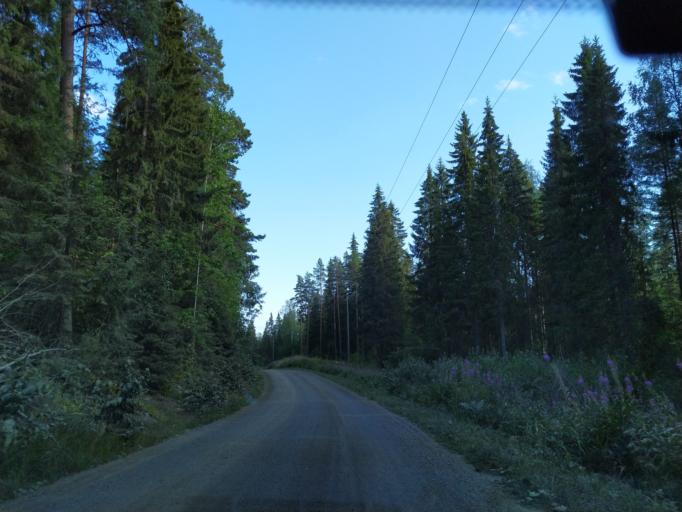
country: FI
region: Central Finland
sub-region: Jaemsae
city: Kuhmoinen
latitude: 61.6990
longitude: 24.9242
